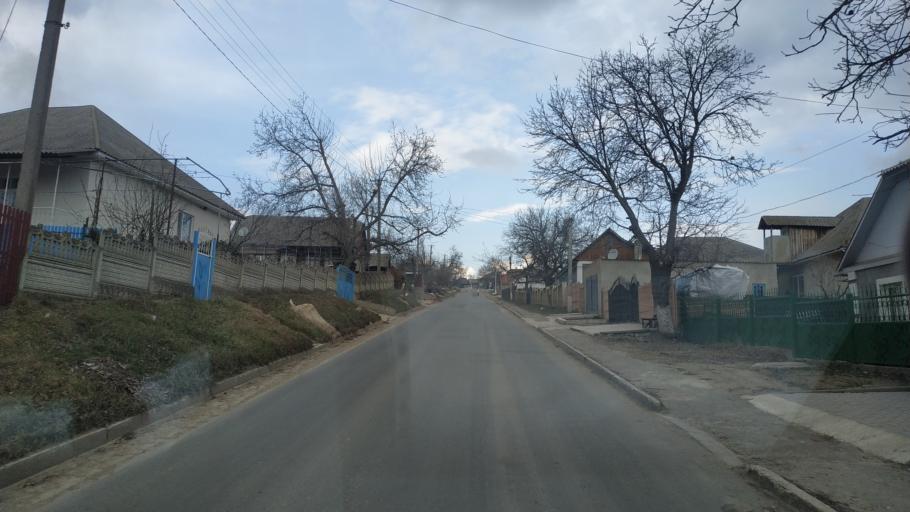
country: MD
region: Anenii Noi
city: Varnita
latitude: 46.8457
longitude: 29.3570
